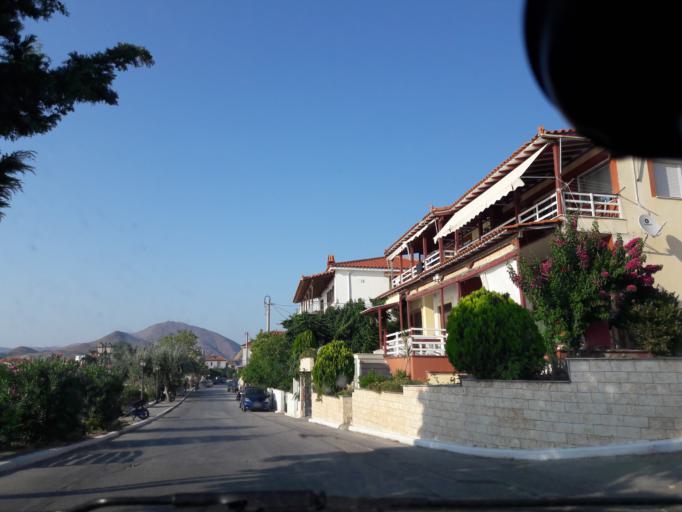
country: GR
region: North Aegean
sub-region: Nomos Lesvou
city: Myrina
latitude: 39.8706
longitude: 25.0604
